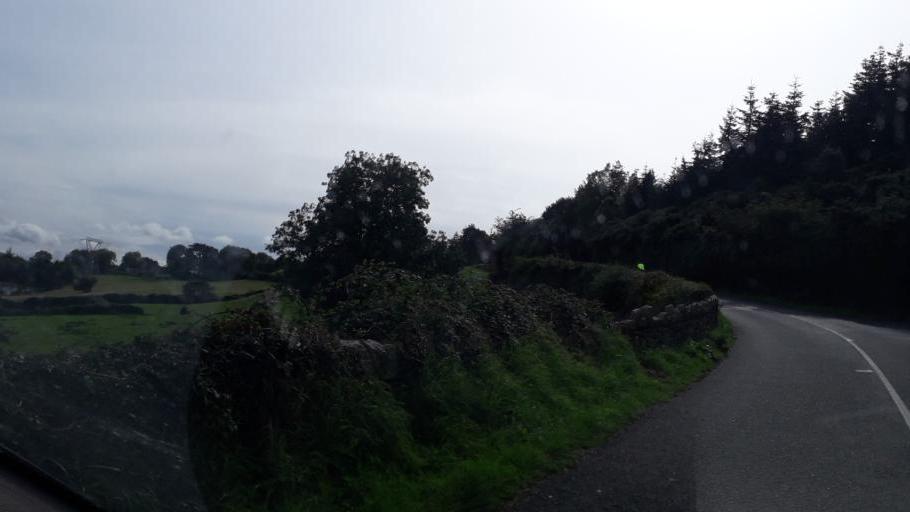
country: IE
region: Leinster
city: Sandyford
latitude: 53.2530
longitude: -6.2193
